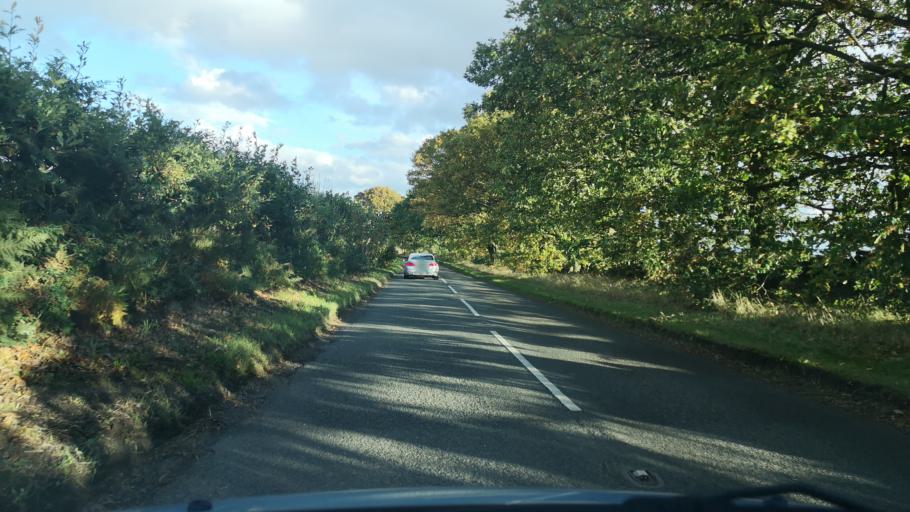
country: GB
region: England
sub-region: City and Borough of Wakefield
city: Woolley
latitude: 53.6205
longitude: -1.5212
